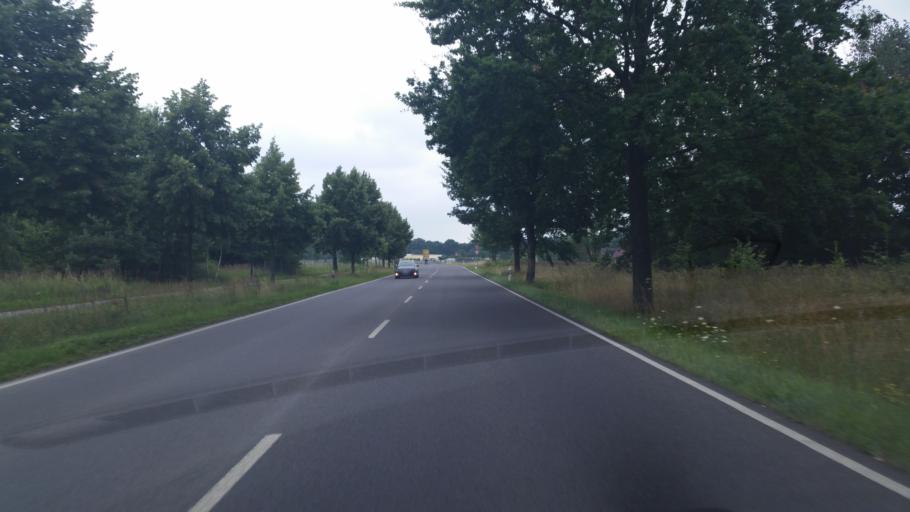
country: DE
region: Brandenburg
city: Senftenberg
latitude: 51.5019
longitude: 14.0637
